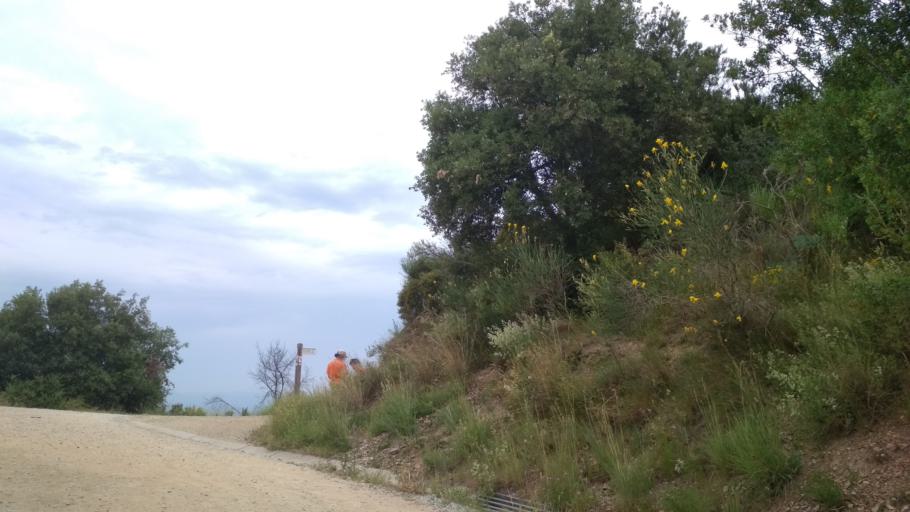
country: ES
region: Catalonia
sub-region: Provincia de Barcelona
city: Nou Barris
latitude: 41.4528
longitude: 2.1640
